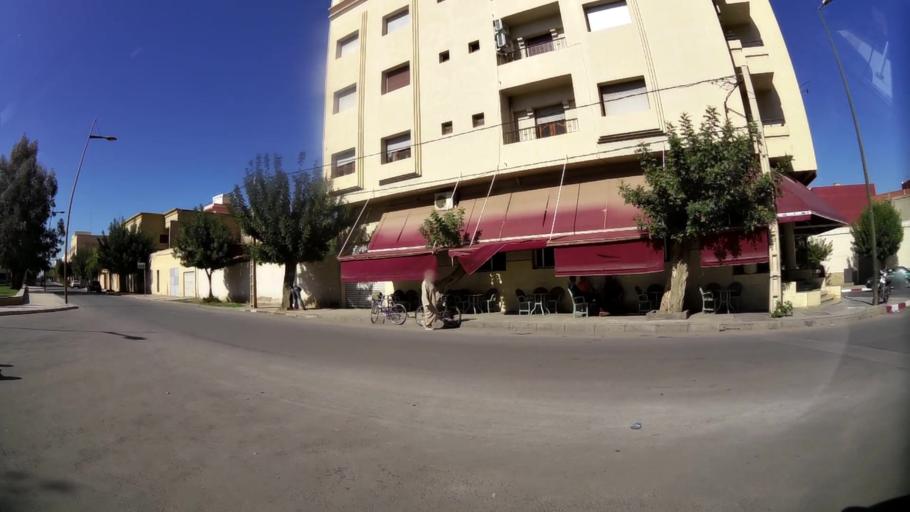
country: MA
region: Oriental
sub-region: Oujda-Angad
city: Oujda
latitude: 34.6858
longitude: -1.9202
